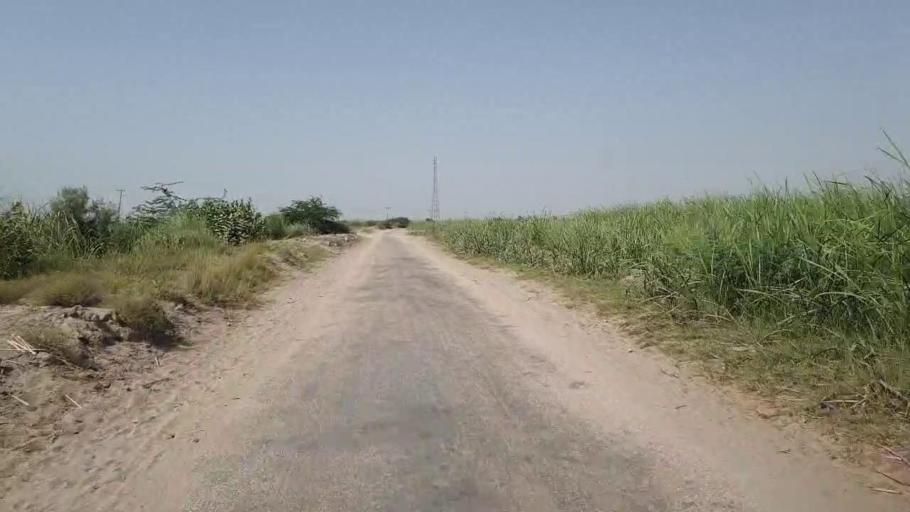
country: PK
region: Sindh
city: Jam Sahib
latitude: 26.4256
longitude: 68.9093
